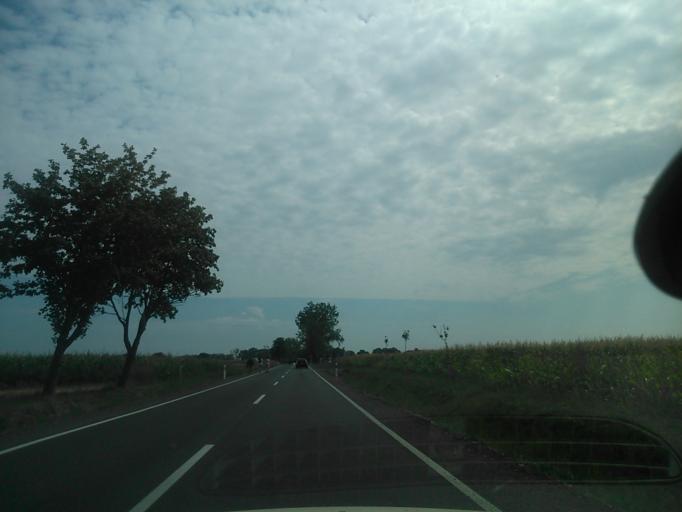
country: PL
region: Warmian-Masurian Voivodeship
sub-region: Powiat dzialdowski
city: Lidzbark
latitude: 53.2324
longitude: 19.9562
